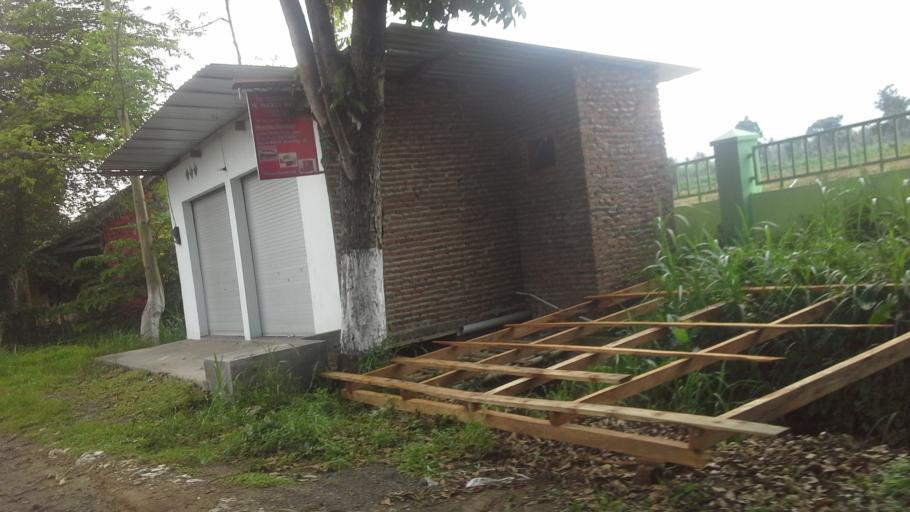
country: ID
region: East Java
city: Krajan Satu Pekauman
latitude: -7.9733
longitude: 113.7983
